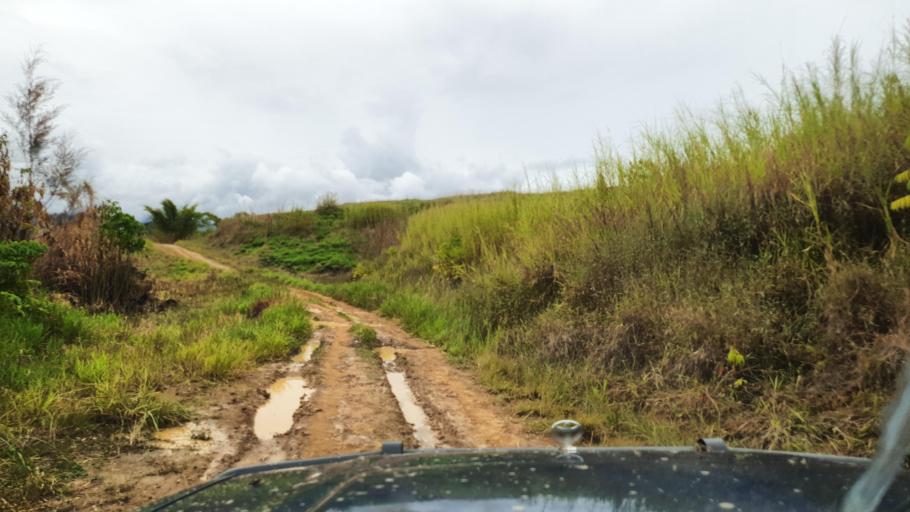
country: PG
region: Jiwaka
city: Minj
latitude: -5.9283
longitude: 144.7457
